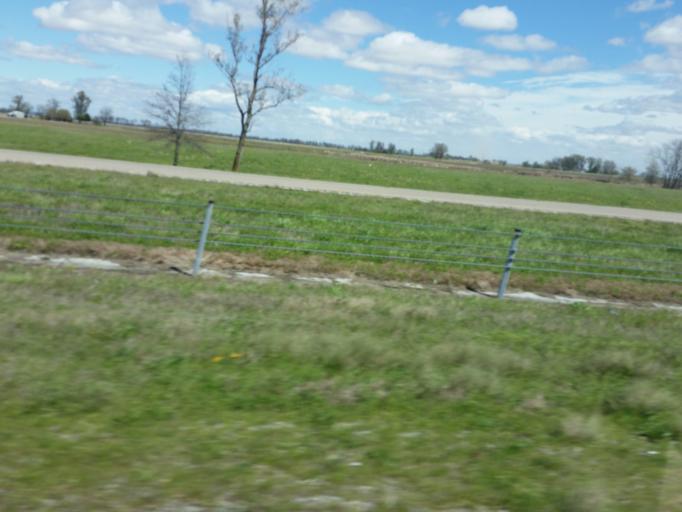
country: US
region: Arkansas
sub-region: Craighead County
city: Bay
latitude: 35.7734
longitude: -90.5828
